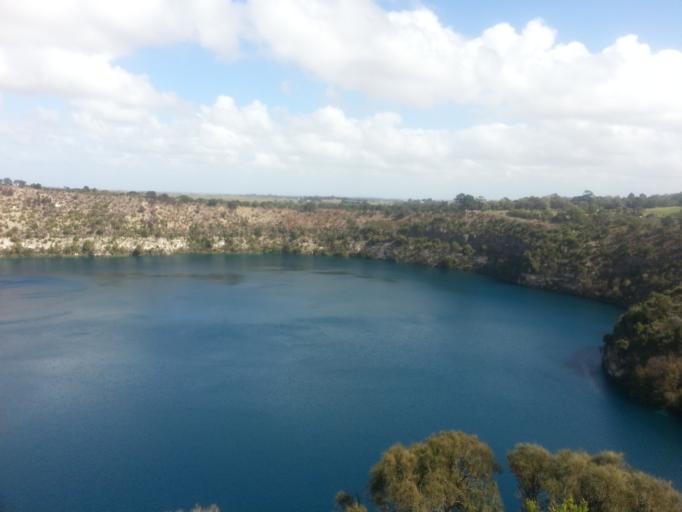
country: AU
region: South Australia
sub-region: Mount Gambier
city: Mount Gambier
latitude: -37.8438
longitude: 140.7785
